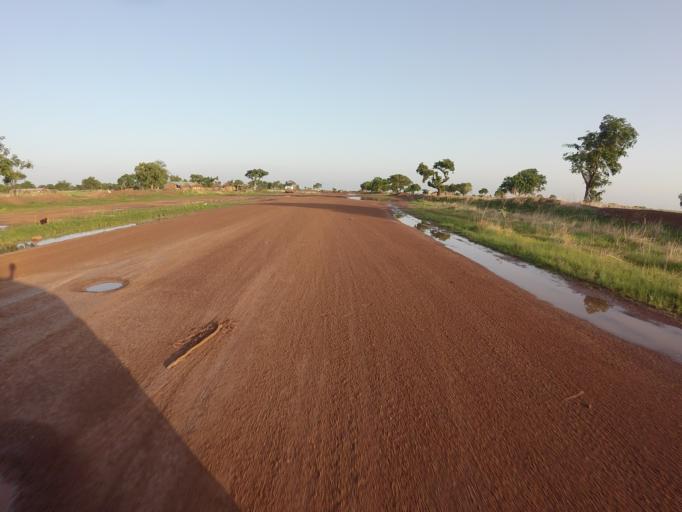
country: TG
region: Savanes
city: Sansanne-Mango
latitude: 10.2307
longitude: -0.0722
